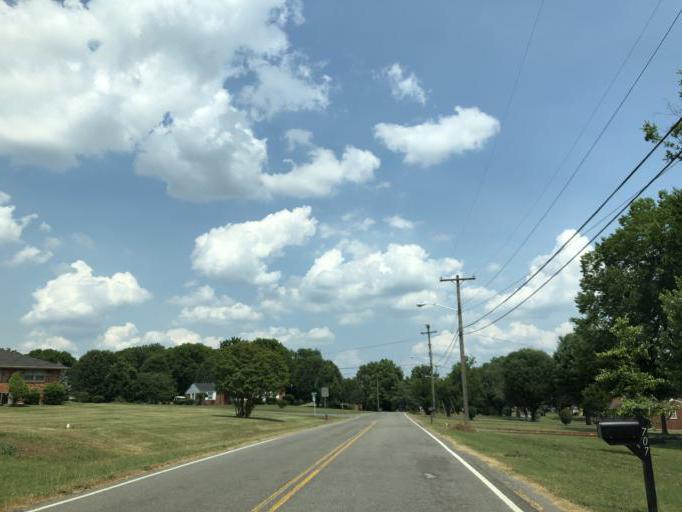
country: US
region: Tennessee
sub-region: Davidson County
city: Goodlettsville
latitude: 36.2458
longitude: -86.7337
